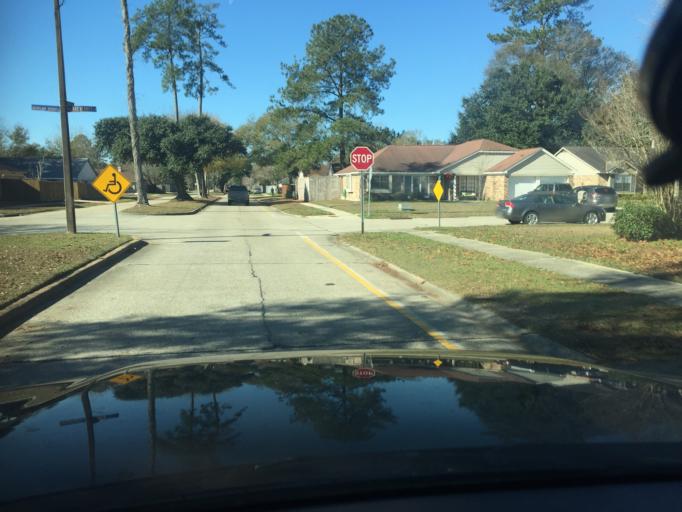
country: US
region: Louisiana
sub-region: Saint Tammany Parish
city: Slidell
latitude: 30.3009
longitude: -89.7297
